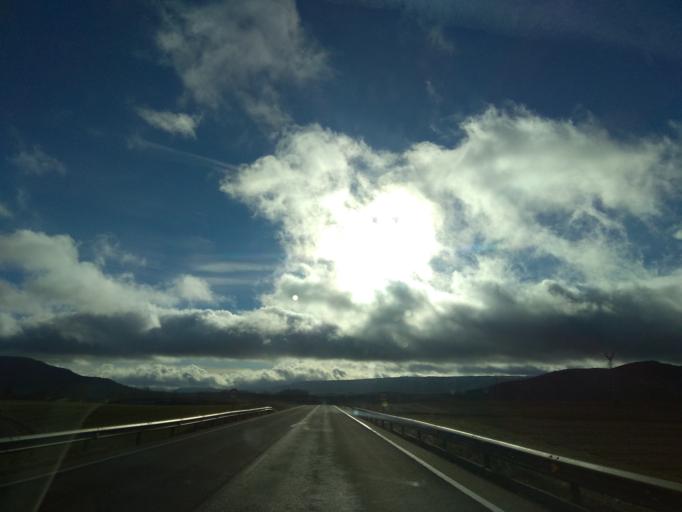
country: ES
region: Castille and Leon
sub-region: Provincia de Palencia
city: Pomar de Valdivia
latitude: 42.7692
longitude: -4.1949
